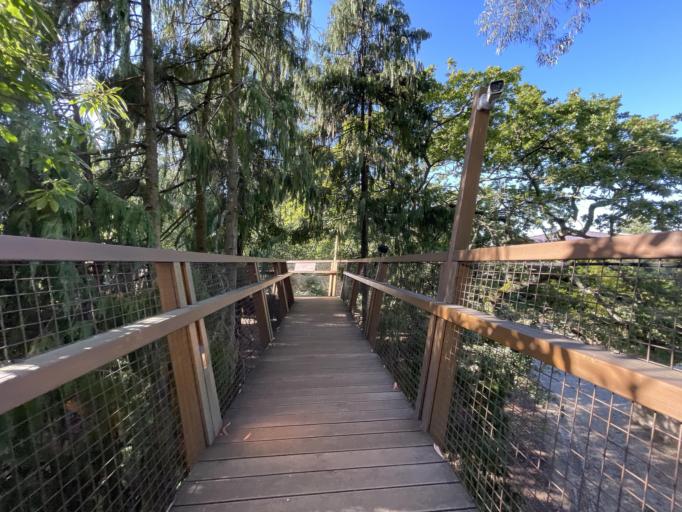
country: PT
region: Porto
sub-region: Matosinhos
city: Senhora da Hora
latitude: 41.1576
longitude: -8.6560
